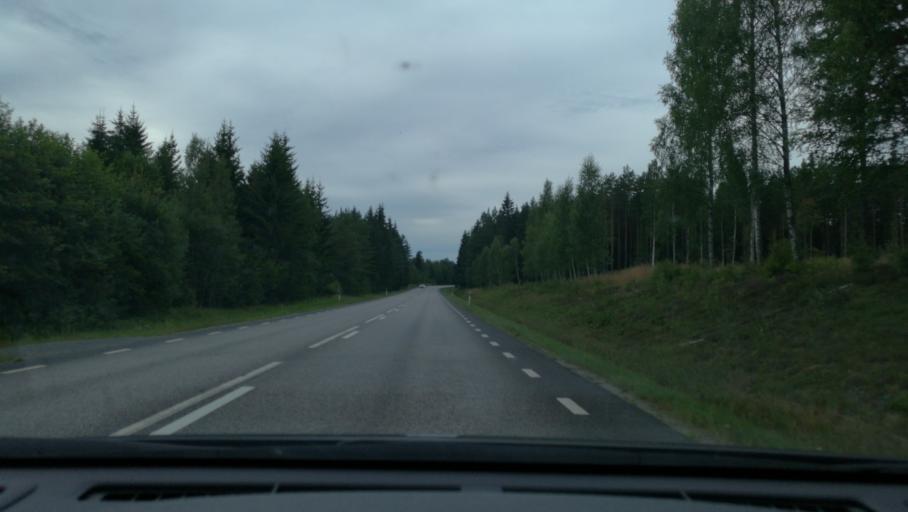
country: SE
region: Soedermanland
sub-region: Katrineholms Kommun
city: Katrineholm
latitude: 59.0750
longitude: 16.2159
